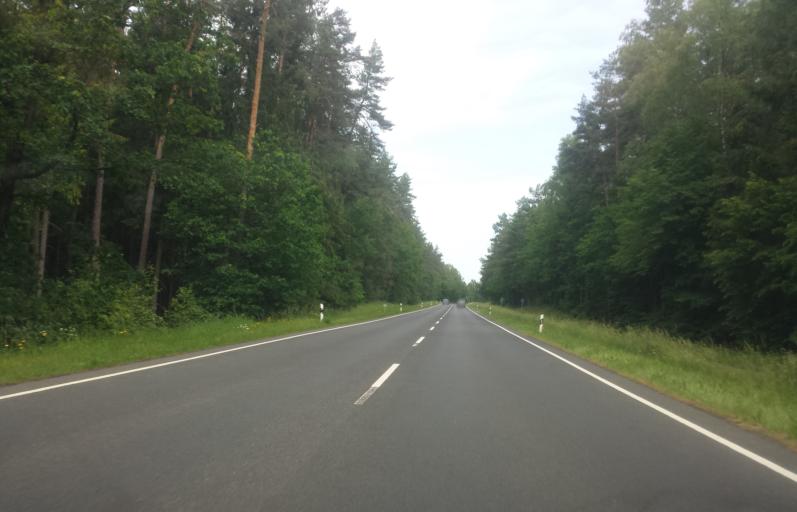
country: DE
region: Bavaria
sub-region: Upper Palatinate
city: Pressath
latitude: 49.7522
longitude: 11.9225
